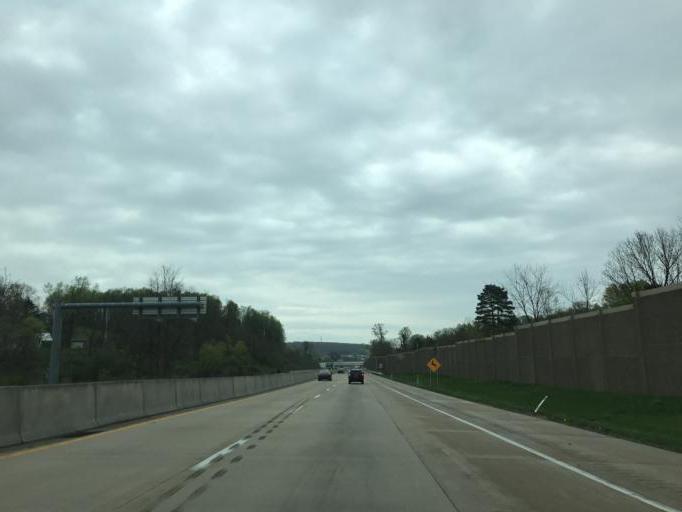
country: US
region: Pennsylvania
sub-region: Berks County
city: Mohnton
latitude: 40.2794
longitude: -76.0183
